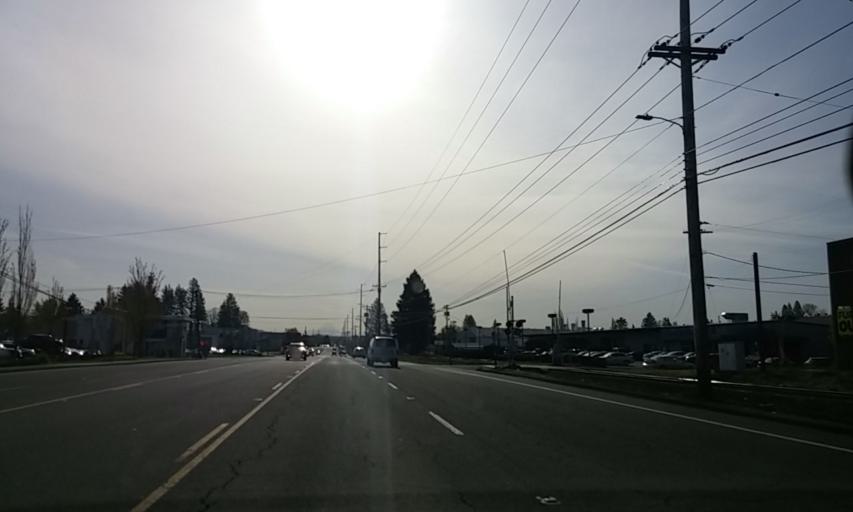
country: US
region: Oregon
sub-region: Washington County
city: Beaverton
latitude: 45.4892
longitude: -122.8232
